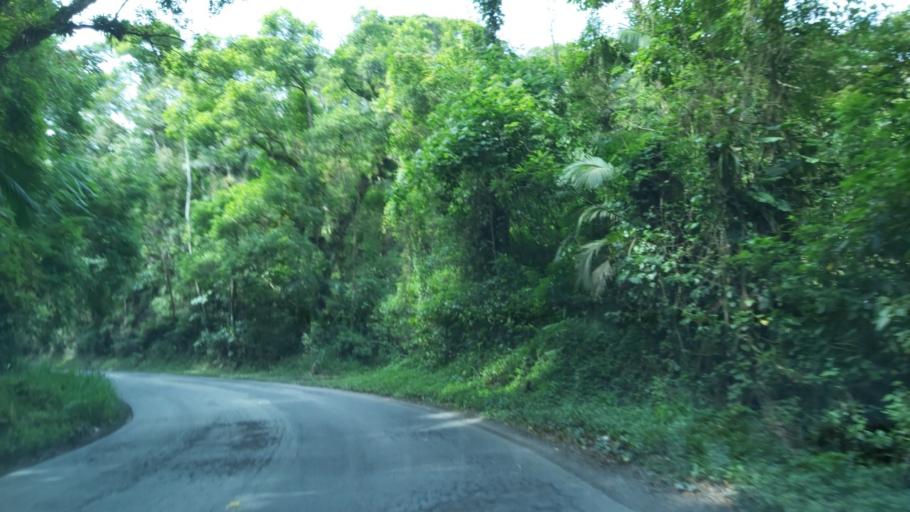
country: BR
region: Sao Paulo
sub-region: Miracatu
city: Miracatu
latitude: -24.0568
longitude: -47.5779
